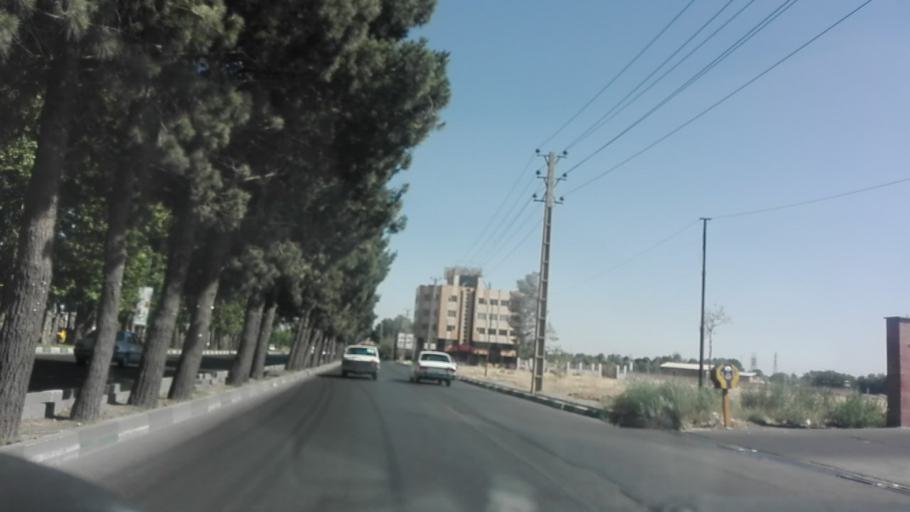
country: IR
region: Tehran
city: Shahriar
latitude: 35.6537
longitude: 51.0507
